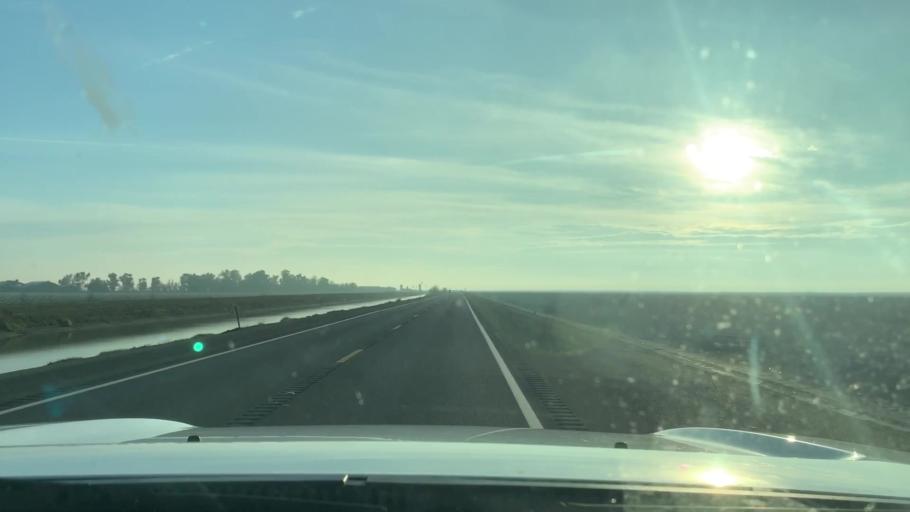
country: US
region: California
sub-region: Kings County
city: Stratford
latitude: 36.1325
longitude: -119.8843
